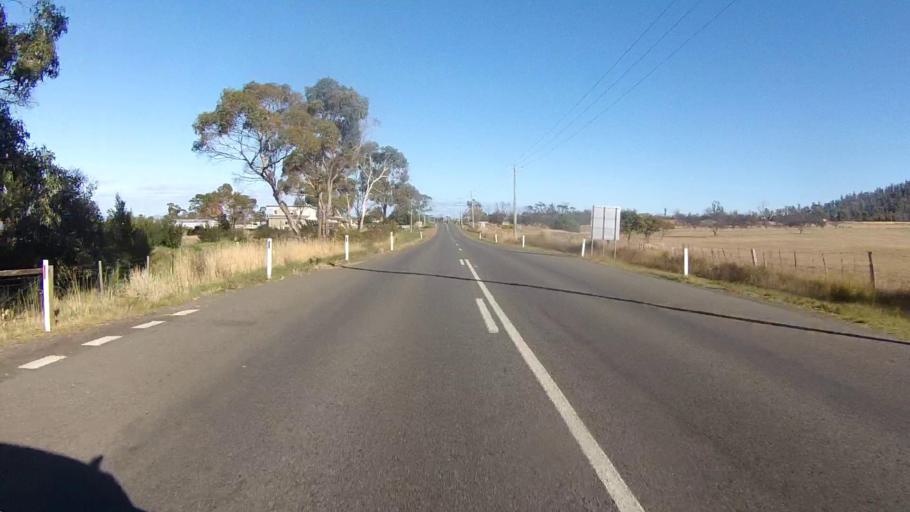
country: AU
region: Tasmania
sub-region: Sorell
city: Sorell
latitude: -42.8771
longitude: 147.8234
